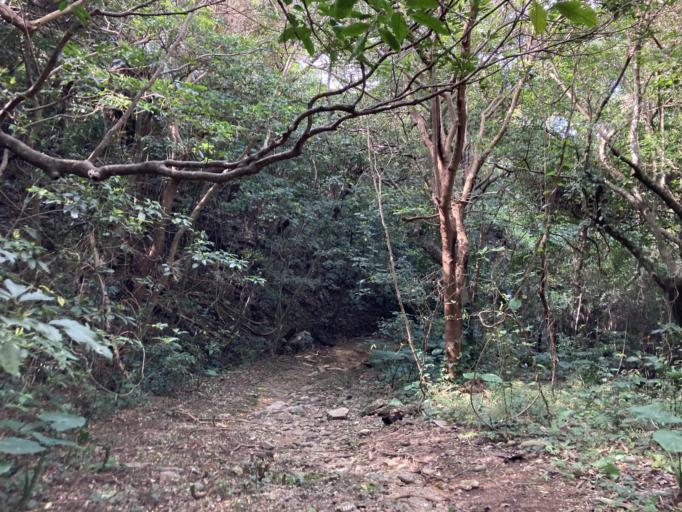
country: JP
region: Okinawa
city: Nago
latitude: 26.6888
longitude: 127.9276
